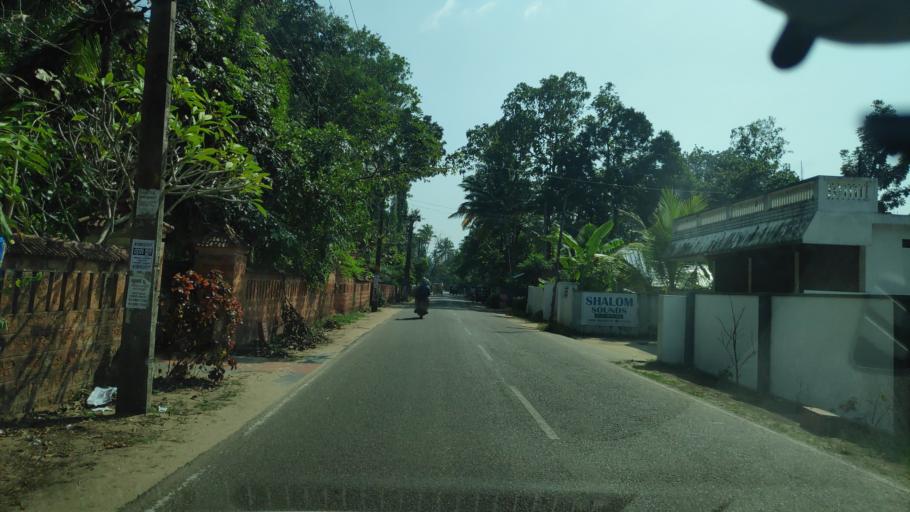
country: IN
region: Kerala
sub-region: Alappuzha
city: Vayalar
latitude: 9.6525
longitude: 76.2995
